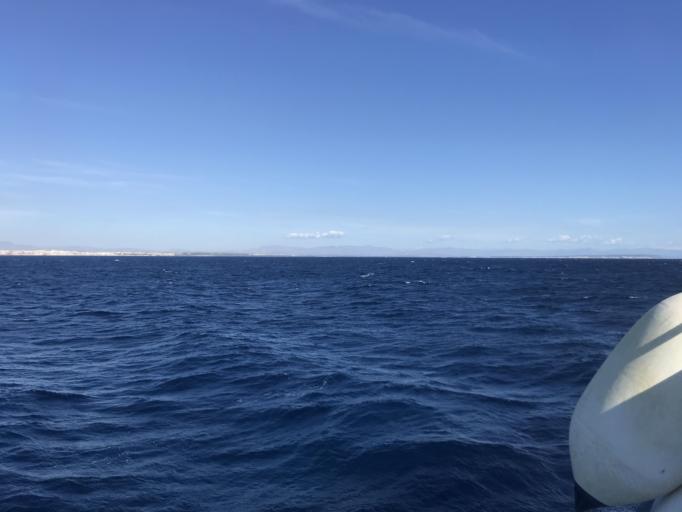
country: ES
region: Valencia
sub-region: Provincia de Alicante
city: Guardamar del Segura
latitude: 38.0340
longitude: -0.6123
